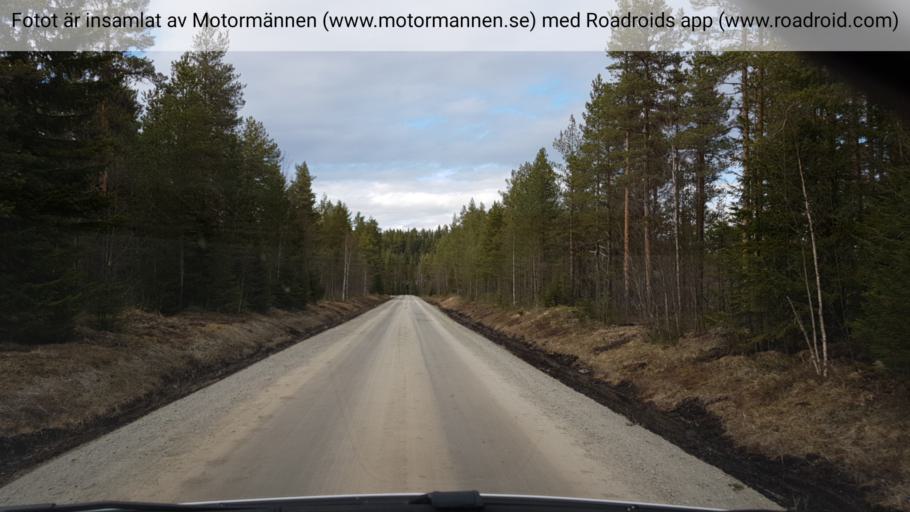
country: SE
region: Jaemtland
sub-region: OEstersunds Kommun
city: Brunflo
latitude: 62.9422
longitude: 14.6660
